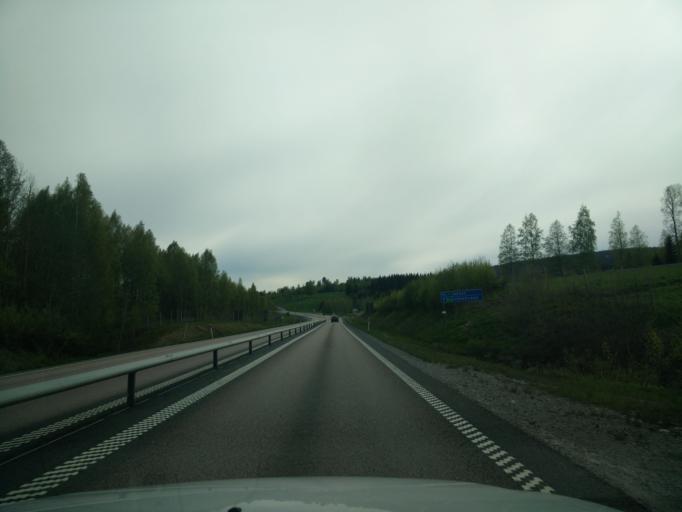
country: SE
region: Vaesternorrland
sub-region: OErnskoeldsviks Kommun
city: Bjasta
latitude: 63.1784
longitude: 18.4434
